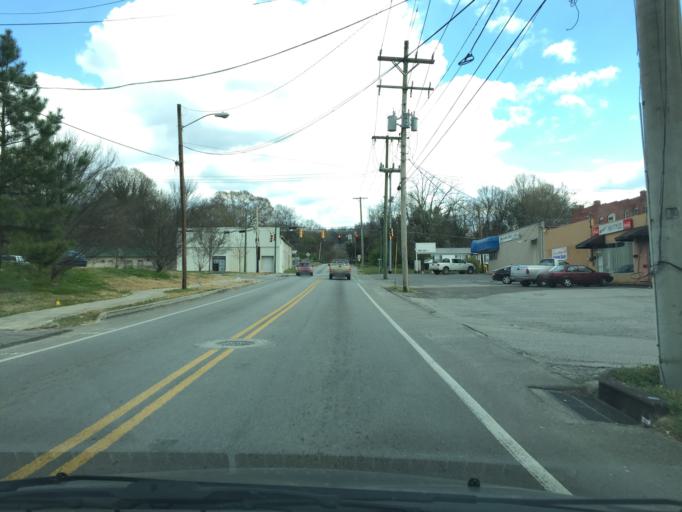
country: US
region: Tennessee
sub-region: Hamilton County
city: East Chattanooga
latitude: 35.0733
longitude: -85.2507
